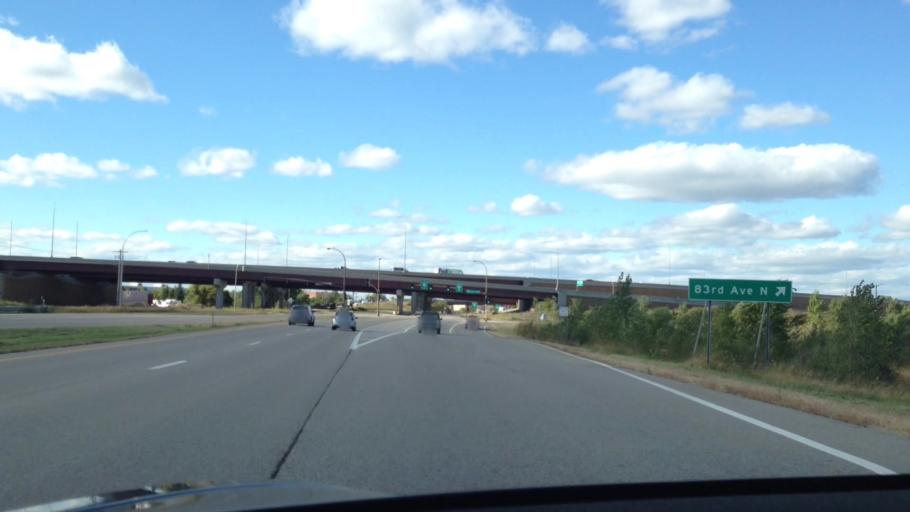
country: US
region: Minnesota
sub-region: Hennepin County
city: Osseo
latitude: 45.1038
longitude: -93.3911
